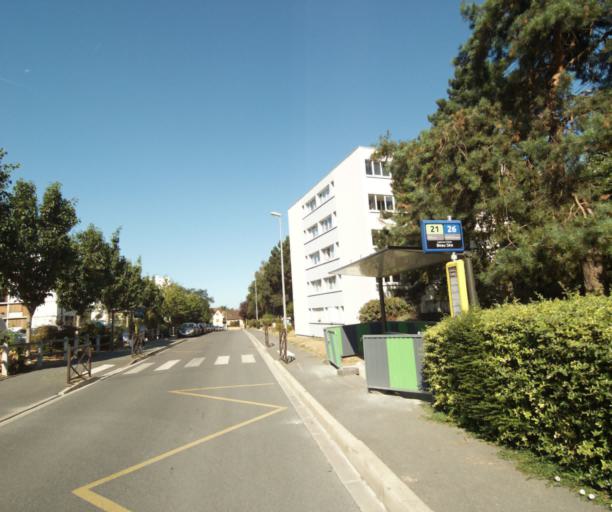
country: FR
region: Ile-de-France
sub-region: Departement de Seine-et-Marne
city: Lagny-sur-Marne
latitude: 48.8698
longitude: 2.7029
